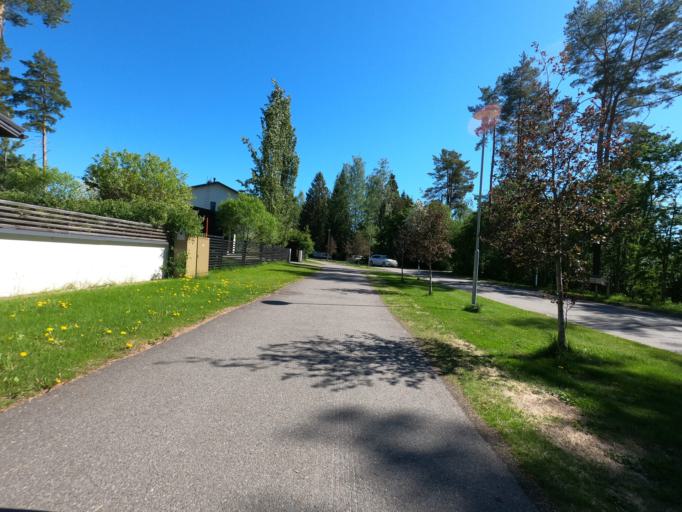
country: FI
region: North Karelia
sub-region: Joensuu
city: Joensuu
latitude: 62.5763
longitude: 29.7684
